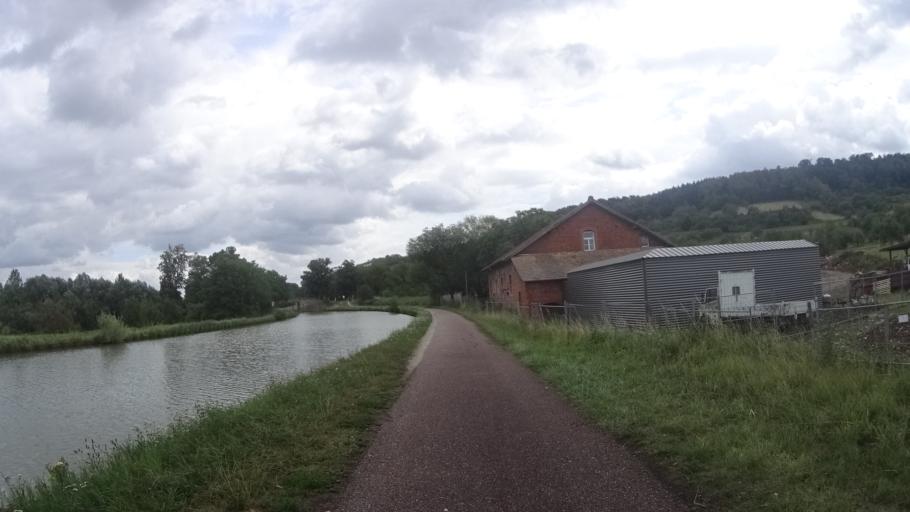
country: FR
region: Alsace
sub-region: Departement du Bas-Rhin
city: Schwindratzheim
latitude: 48.7473
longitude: 7.6006
